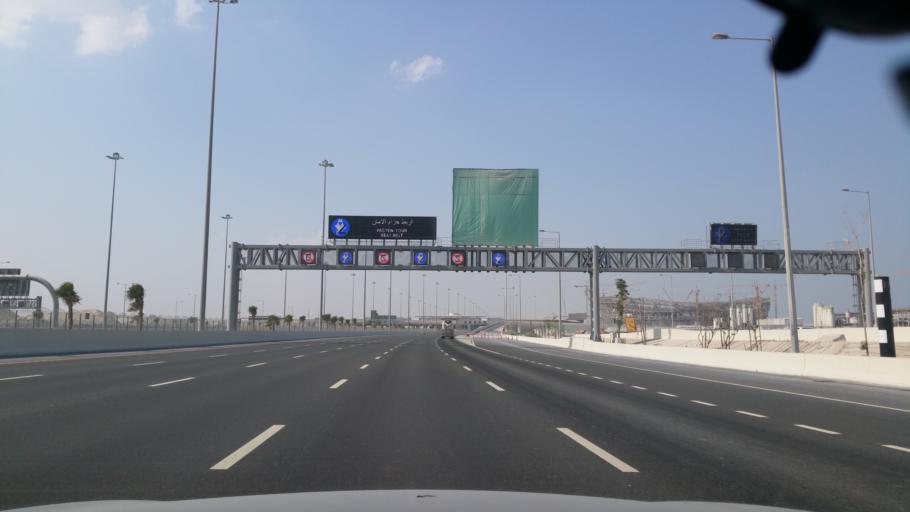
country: QA
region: Baladiyat Umm Salal
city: Umm Salal Muhammad
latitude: 25.4071
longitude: 51.4903
